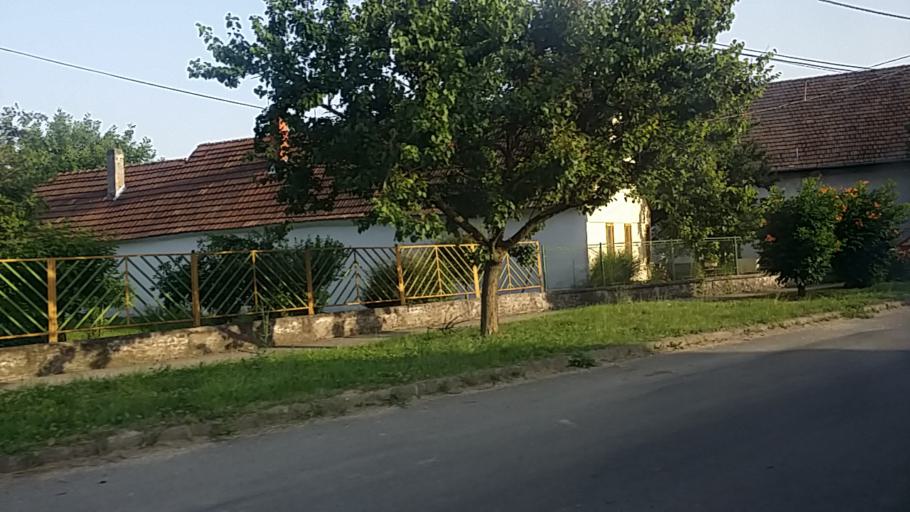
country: HU
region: Baranya
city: Villany
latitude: 45.8713
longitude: 18.4604
